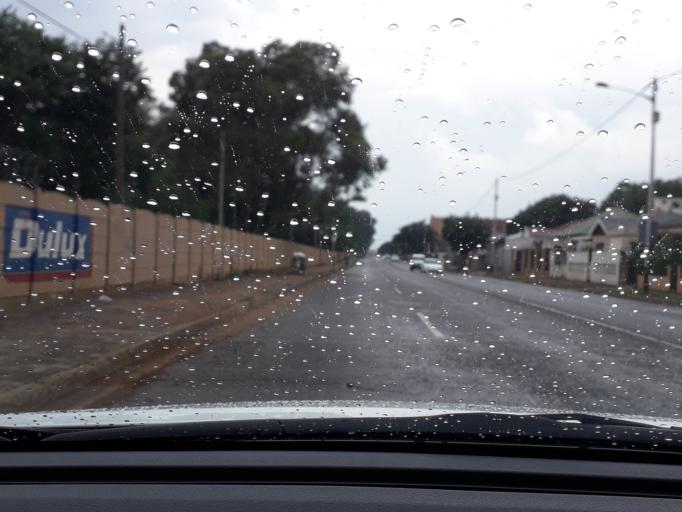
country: ZA
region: Gauteng
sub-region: City of Johannesburg Metropolitan Municipality
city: Johannesburg
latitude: -26.2411
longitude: 28.0441
